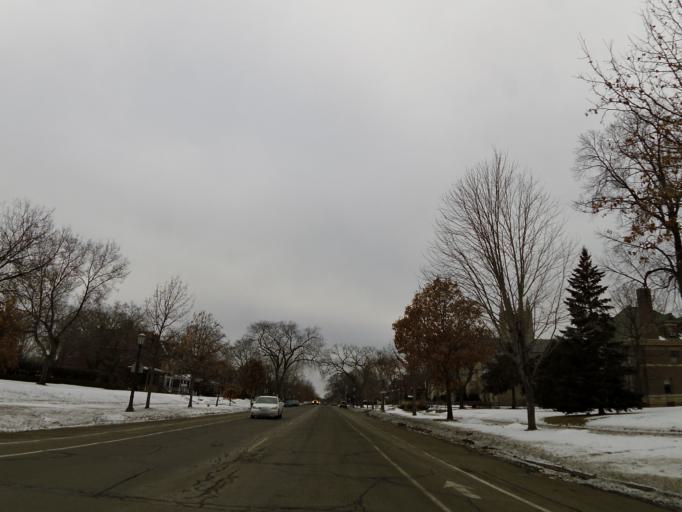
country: US
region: Minnesota
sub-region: Ramsey County
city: Saint Paul
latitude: 44.9414
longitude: -93.1314
